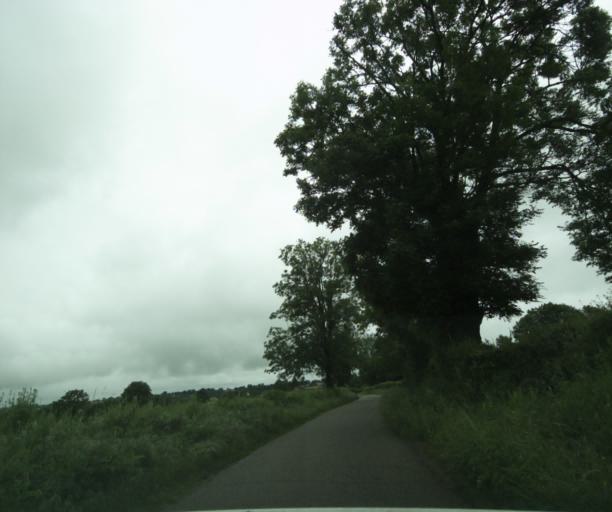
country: FR
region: Bourgogne
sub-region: Departement de Saone-et-Loire
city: Charolles
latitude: 46.4346
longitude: 4.3455
